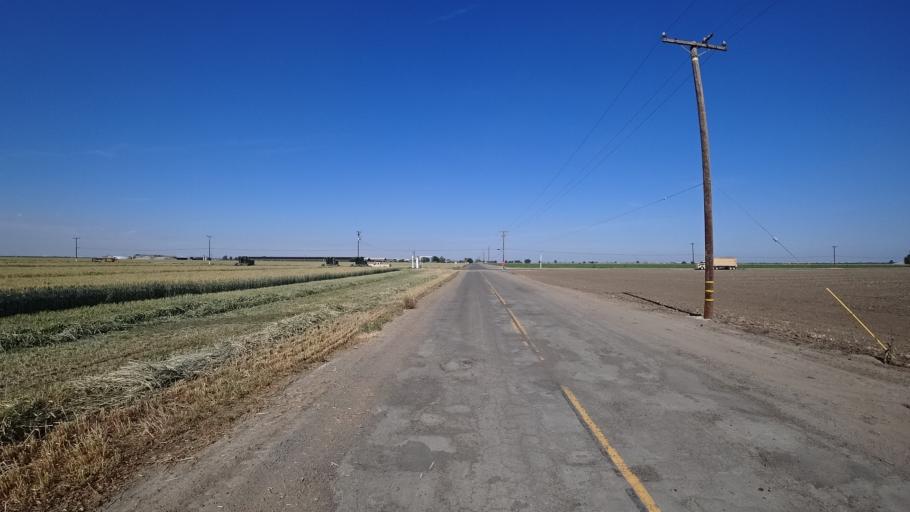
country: US
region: California
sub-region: Kings County
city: Home Garden
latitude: 36.2261
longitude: -119.5461
